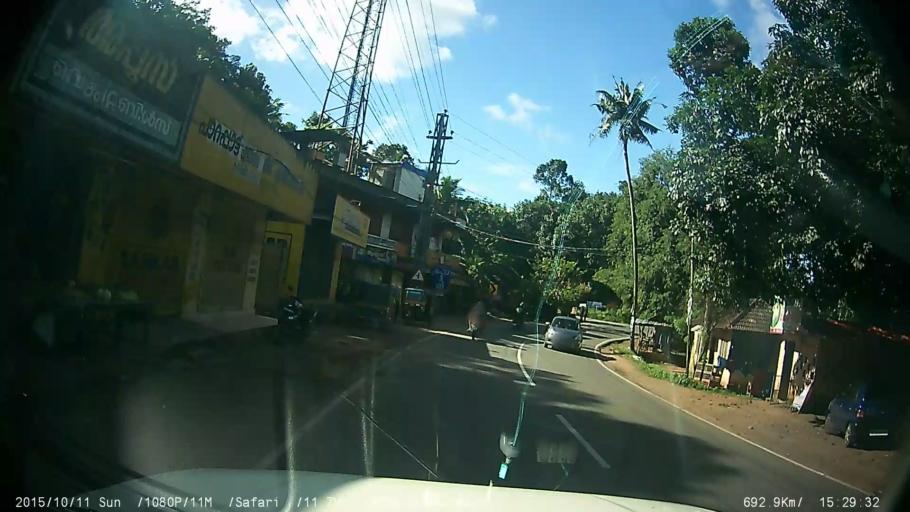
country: IN
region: Kerala
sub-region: Kottayam
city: Changanacheri
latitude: 9.4973
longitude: 76.5727
